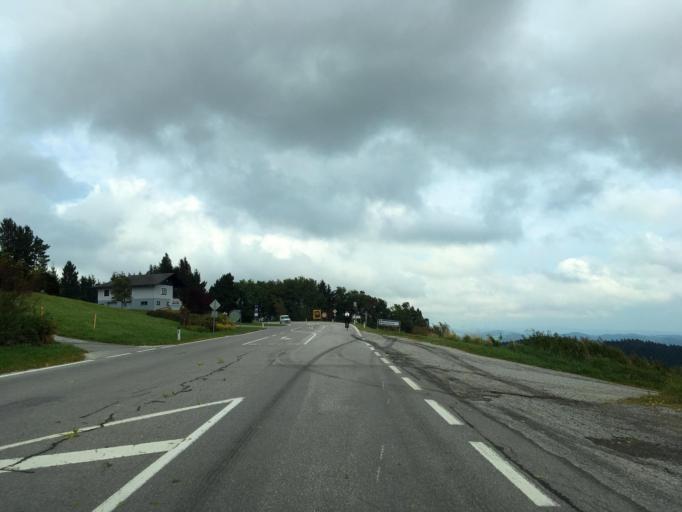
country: AT
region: Lower Austria
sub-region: Politischer Bezirk Neunkirchen
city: Monichkirchen
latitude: 47.5086
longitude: 16.0347
